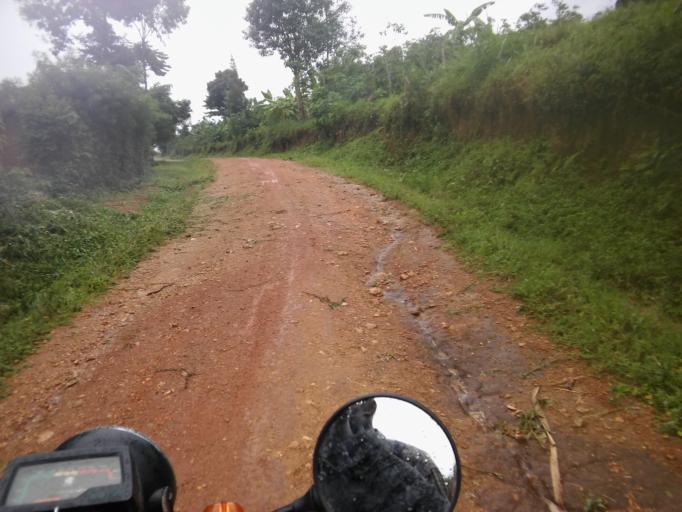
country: UG
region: Eastern Region
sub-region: Bududa District
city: Bududa
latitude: 0.9999
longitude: 34.2379
